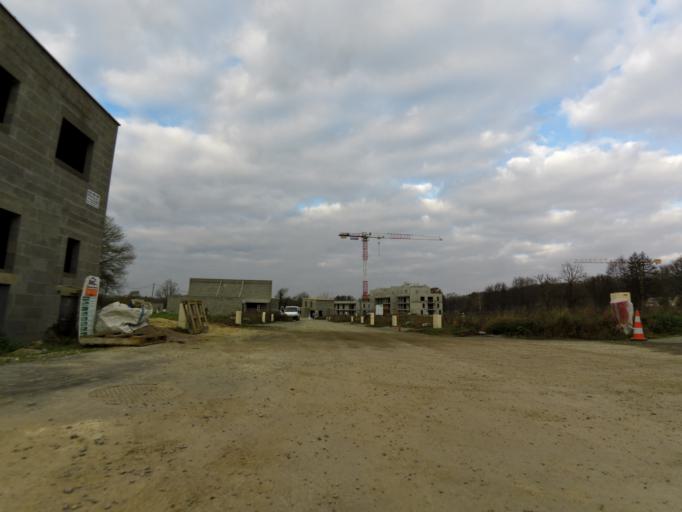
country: FR
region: Brittany
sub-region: Departement d'Ille-et-Vilaine
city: Orgeres
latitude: 47.9942
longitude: -1.6730
